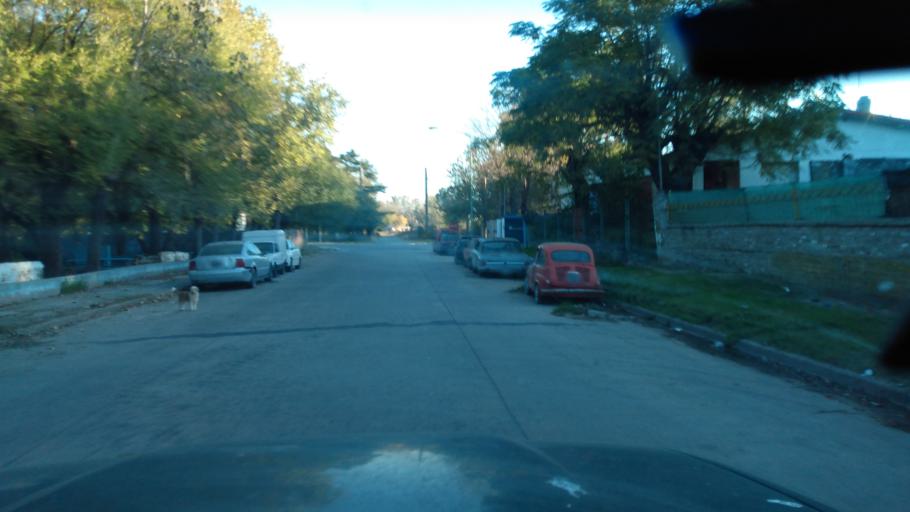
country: AR
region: Buenos Aires
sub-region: Partido de Lujan
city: Lujan
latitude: -34.5662
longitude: -59.1247
